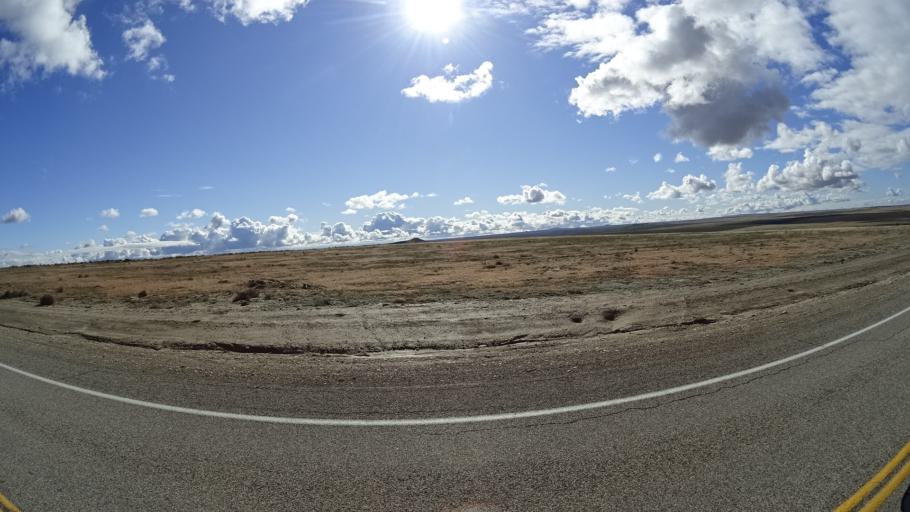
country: US
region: Idaho
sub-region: Ada County
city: Kuna
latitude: 43.3245
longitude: -116.4140
